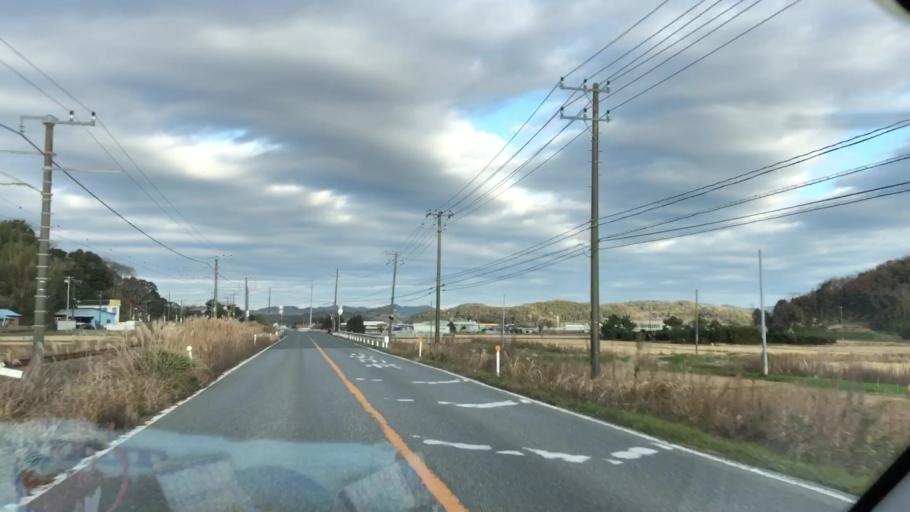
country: JP
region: Chiba
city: Tateyama
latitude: 34.9948
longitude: 139.9192
